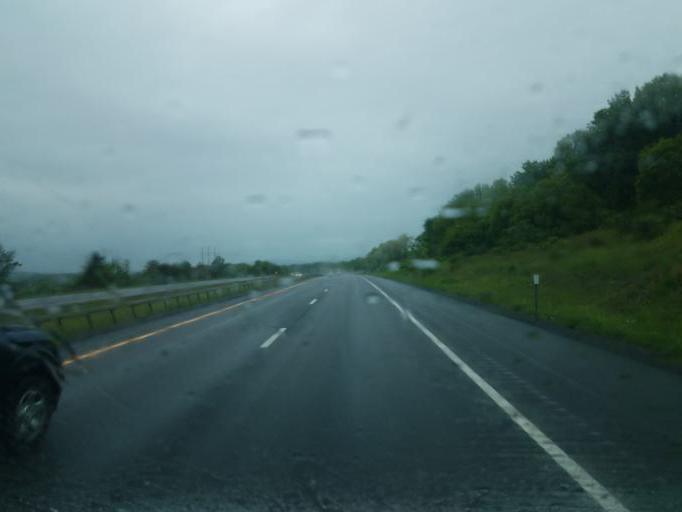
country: US
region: New York
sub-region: Herkimer County
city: Frankfort
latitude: 43.0475
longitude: -75.0589
